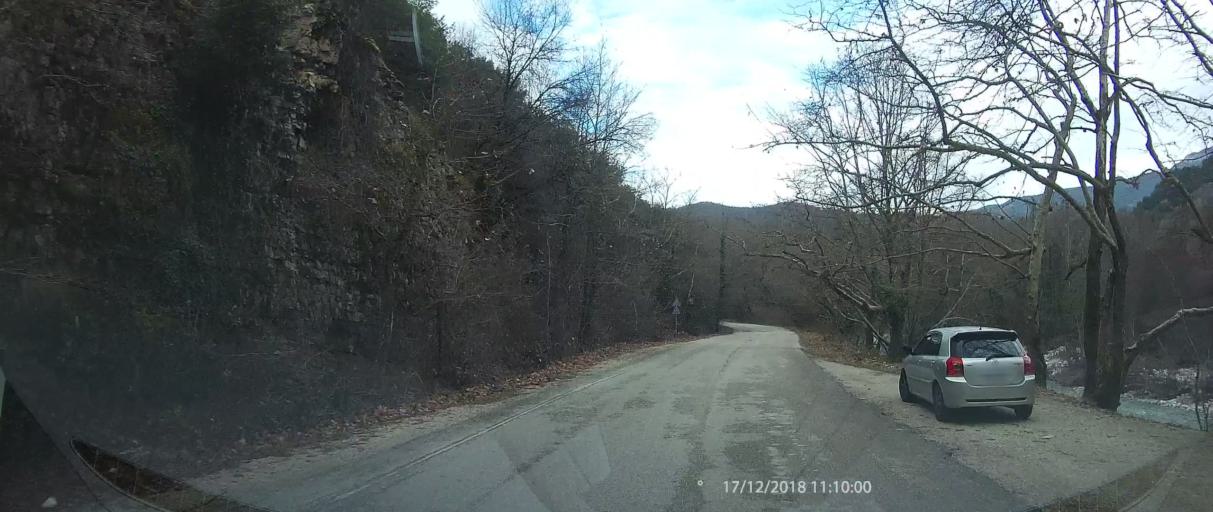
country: GR
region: Epirus
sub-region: Nomos Ioanninon
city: Kalpaki
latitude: 39.9444
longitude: 20.6873
